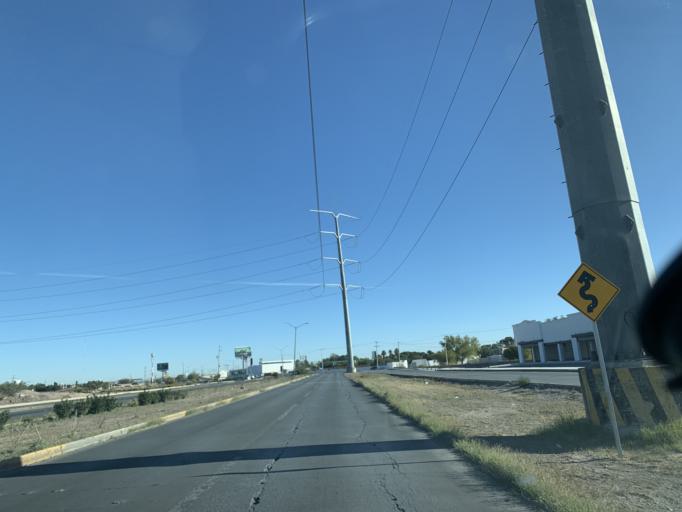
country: US
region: Texas
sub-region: El Paso County
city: Socorro
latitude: 31.6866
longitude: -106.3866
